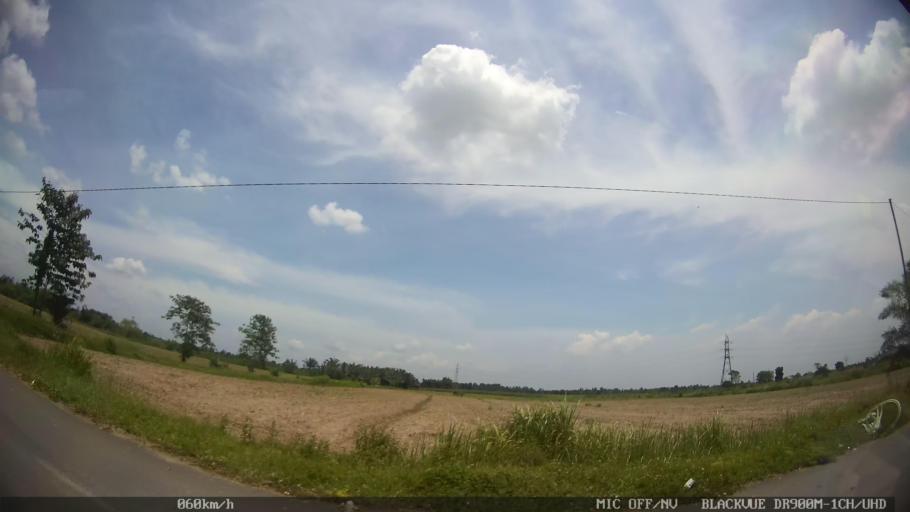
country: ID
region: North Sumatra
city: Binjai
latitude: 3.5913
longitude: 98.5262
